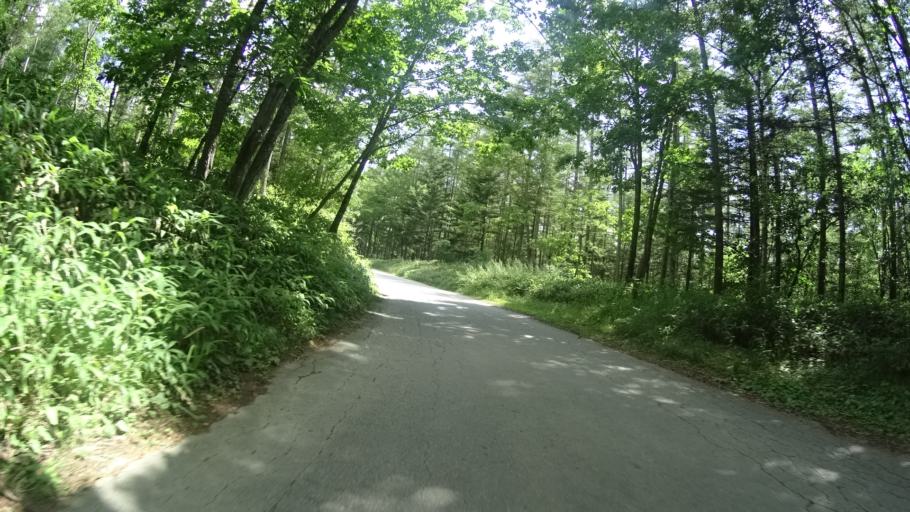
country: JP
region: Yamanashi
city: Enzan
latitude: 35.8218
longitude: 138.6485
